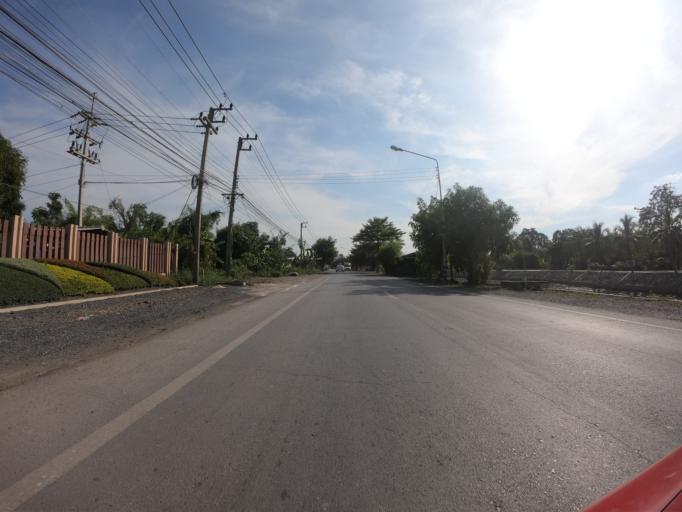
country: TH
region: Pathum Thani
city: Thanyaburi
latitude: 13.9979
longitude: 100.7305
